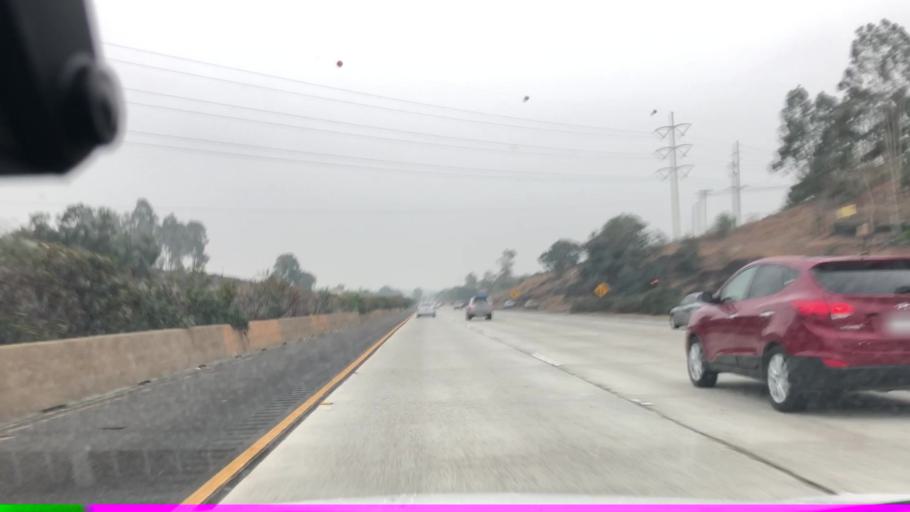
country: US
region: California
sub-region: San Diego County
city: Escondido
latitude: 33.1453
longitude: -117.1046
